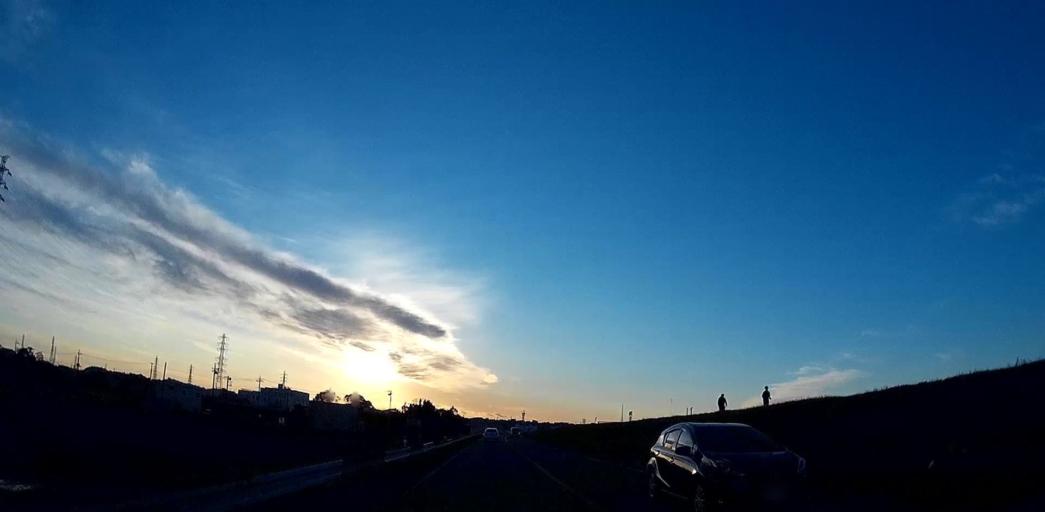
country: JP
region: Chiba
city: Katori-shi
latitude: 35.8967
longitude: 140.5147
